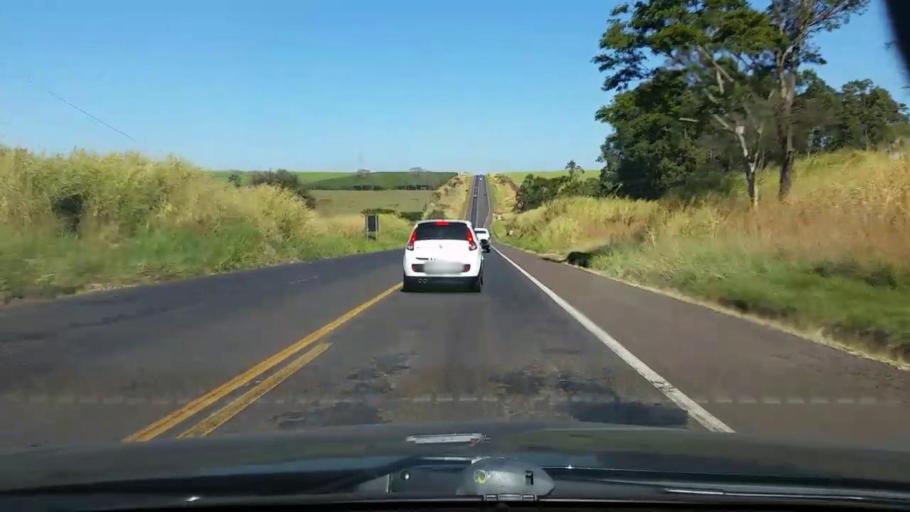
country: BR
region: Sao Paulo
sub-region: Jau
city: Jau
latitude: -22.3462
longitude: -48.5724
